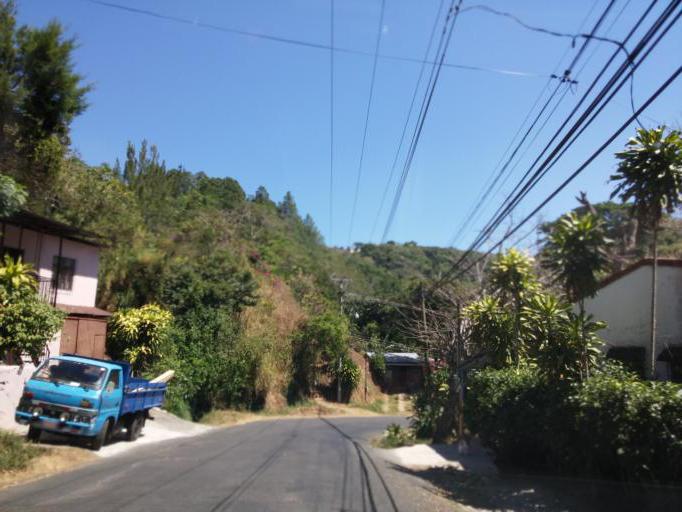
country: CR
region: Alajuela
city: Sabanilla
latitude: 10.0511
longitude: -84.2153
